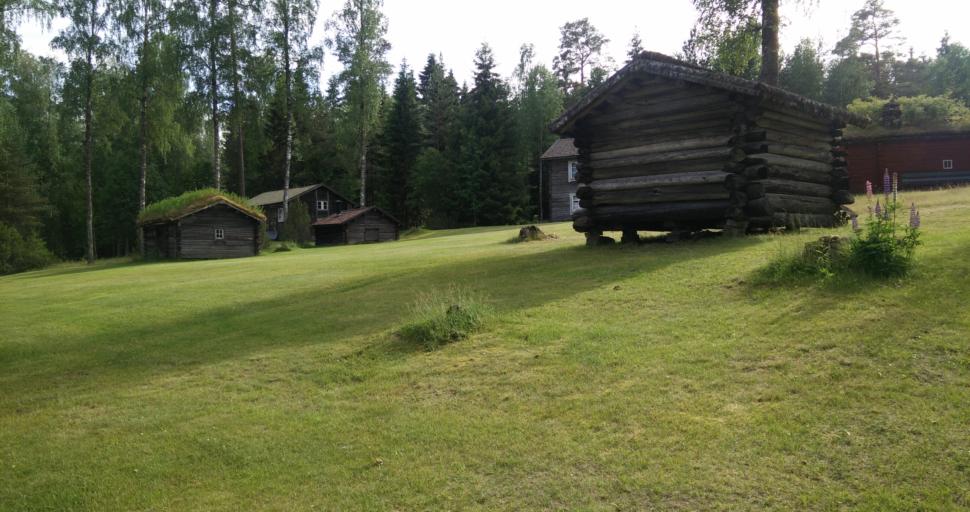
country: SE
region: Vaermland
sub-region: Hagfors Kommun
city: Hagfors
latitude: 59.9955
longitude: 13.5676
